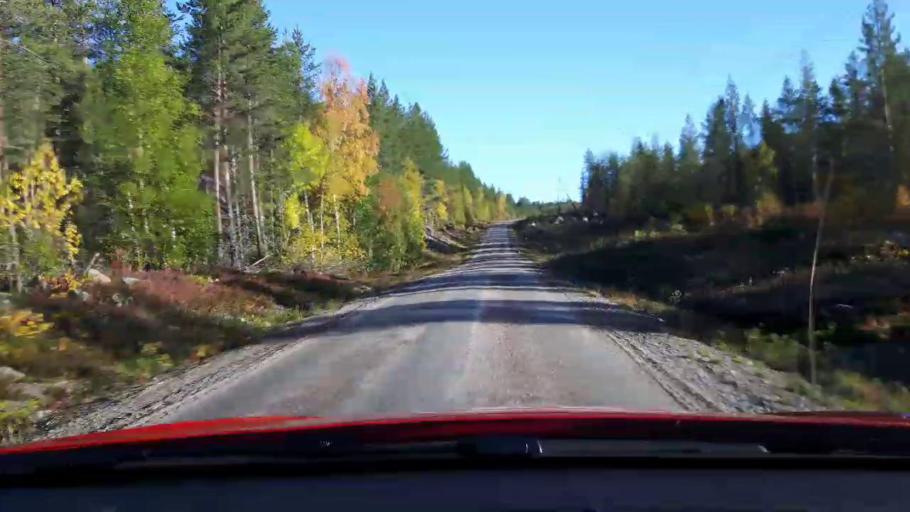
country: SE
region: Jaemtland
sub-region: Stroemsunds Kommun
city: Stroemsund
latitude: 64.3820
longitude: 15.1489
